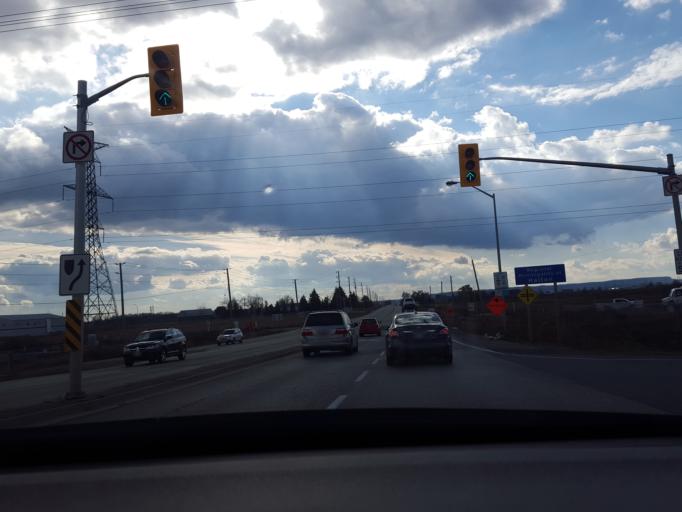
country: CA
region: Ontario
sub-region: Halton
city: Milton
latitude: 43.5707
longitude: -79.7911
